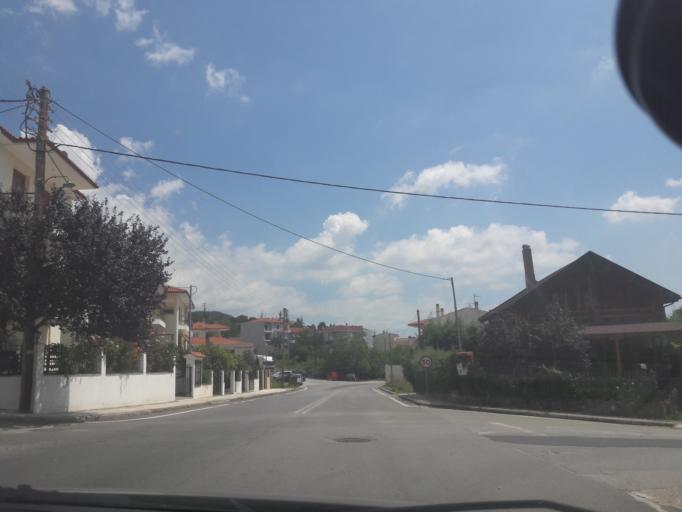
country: GR
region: Central Macedonia
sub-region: Nomos Chalkidikis
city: Polygyros
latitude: 40.3778
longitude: 23.4495
